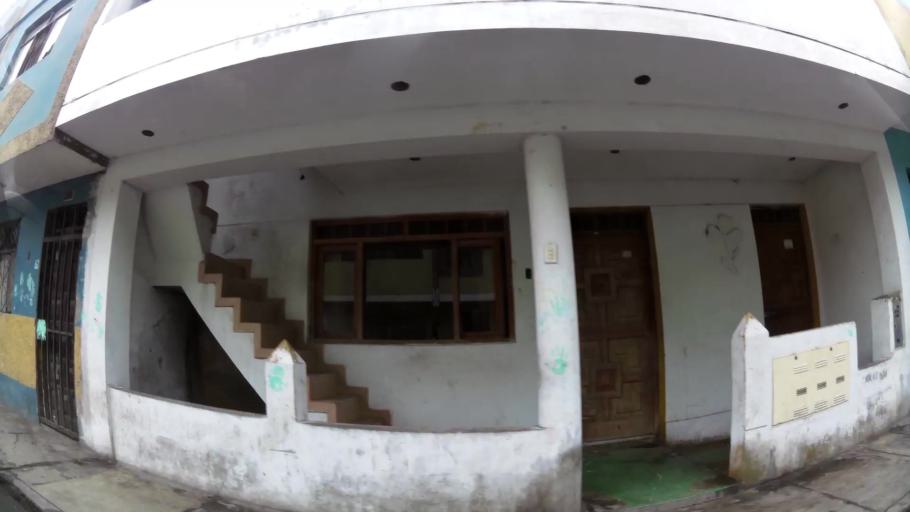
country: PE
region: Lima
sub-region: Lima
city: San Luis
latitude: -12.0549
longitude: -77.0024
